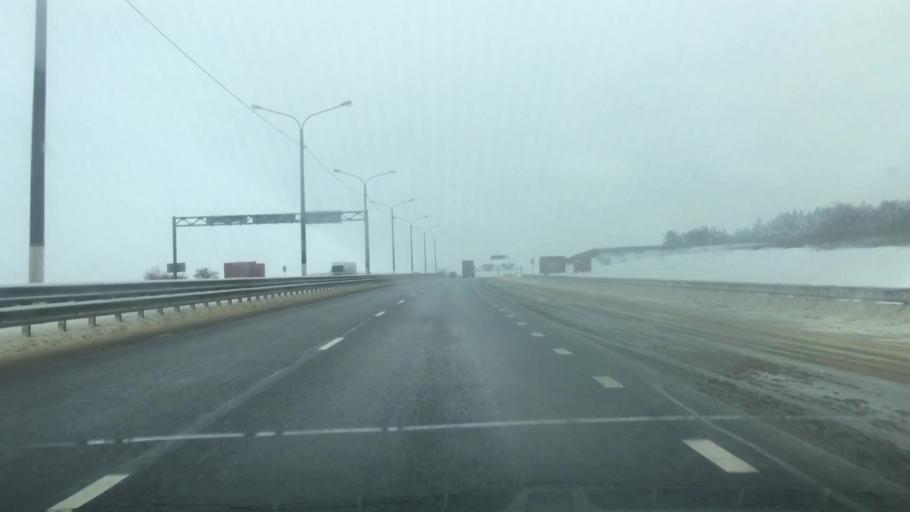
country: RU
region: Tula
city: Yefremov
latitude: 53.1596
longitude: 38.2495
